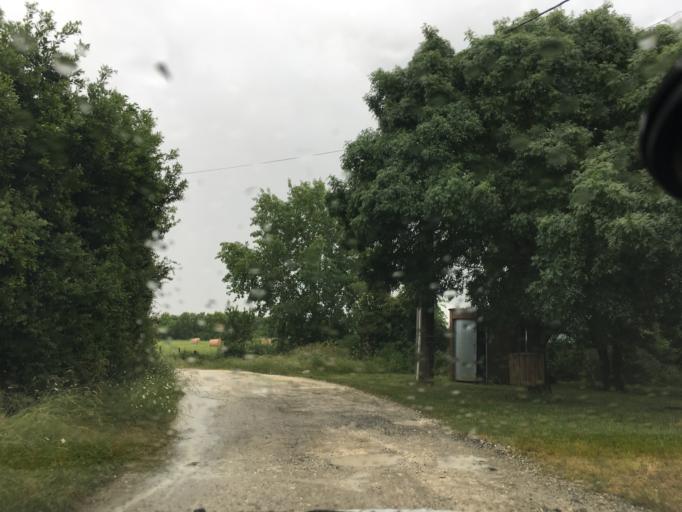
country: FR
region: Aquitaine
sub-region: Departement de la Gironde
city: Saint-Estephe
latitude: 45.3376
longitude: -0.8016
